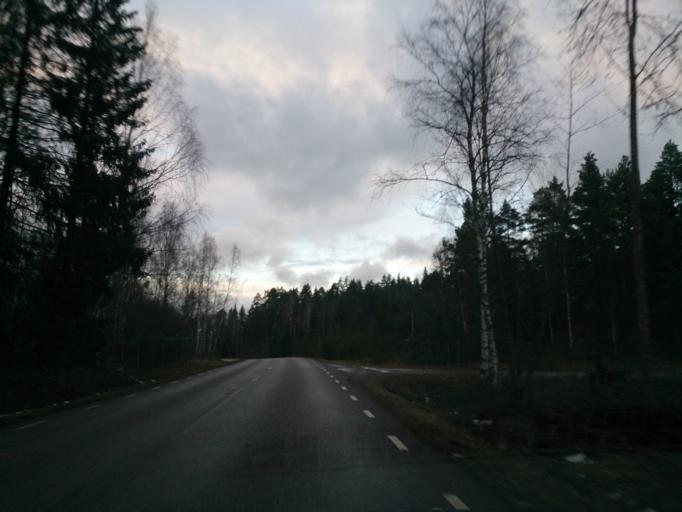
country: SE
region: OEstergoetland
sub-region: Atvidabergs Kommun
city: Atvidaberg
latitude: 58.2689
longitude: 16.0336
